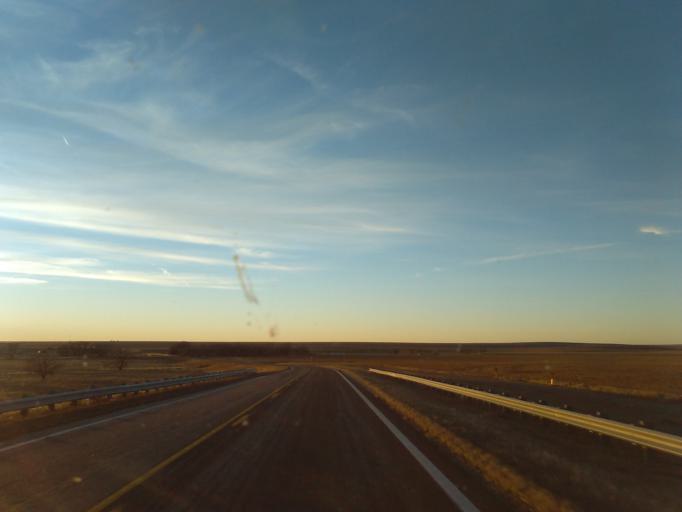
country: US
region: Kansas
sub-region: Wallace County
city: Sharon Springs
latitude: 38.9062
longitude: -101.6204
